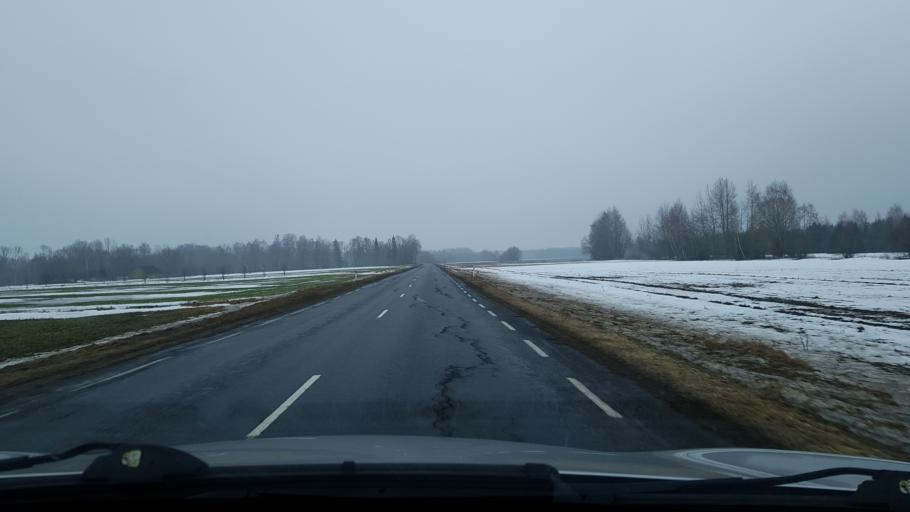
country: EE
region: Valgamaa
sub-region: Torva linn
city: Torva
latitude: 58.1906
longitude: 25.9511
